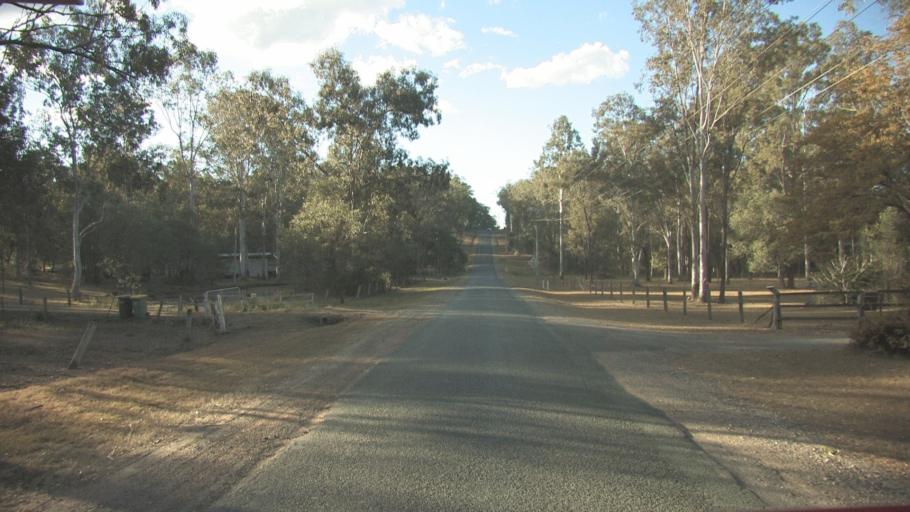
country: AU
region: Queensland
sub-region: Logan
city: Cedar Vale
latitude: -27.8549
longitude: 153.0886
